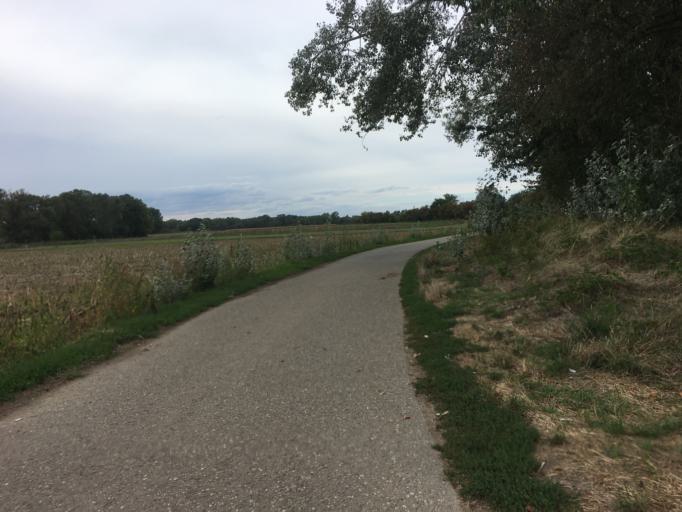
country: DE
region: Baden-Wuerttemberg
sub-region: Karlsruhe Region
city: Bruhl
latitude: 49.3969
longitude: 8.5262
